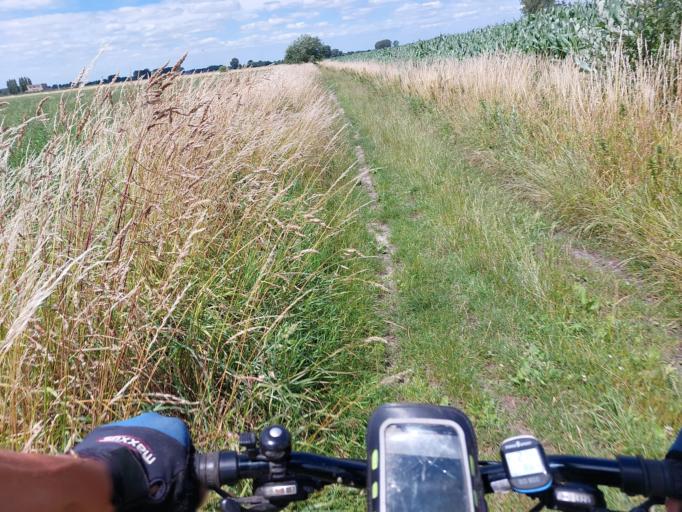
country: BE
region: Wallonia
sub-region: Province du Hainaut
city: Jurbise
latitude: 50.5431
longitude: 3.9392
